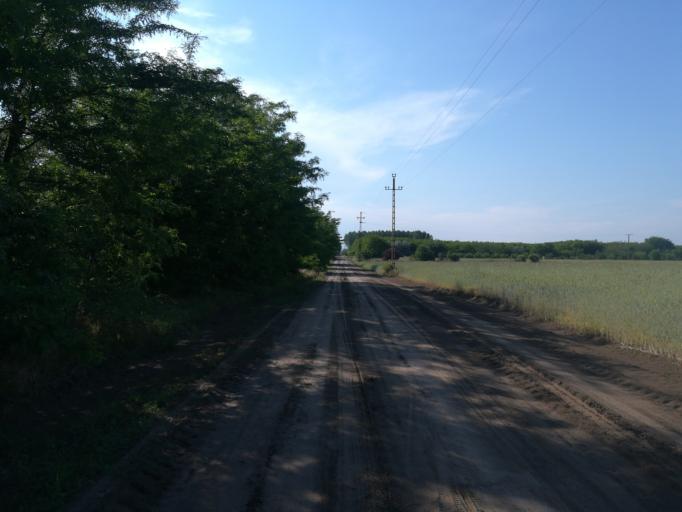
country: HU
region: Bacs-Kiskun
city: Tiszakecske
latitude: 46.9431
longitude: 20.0870
